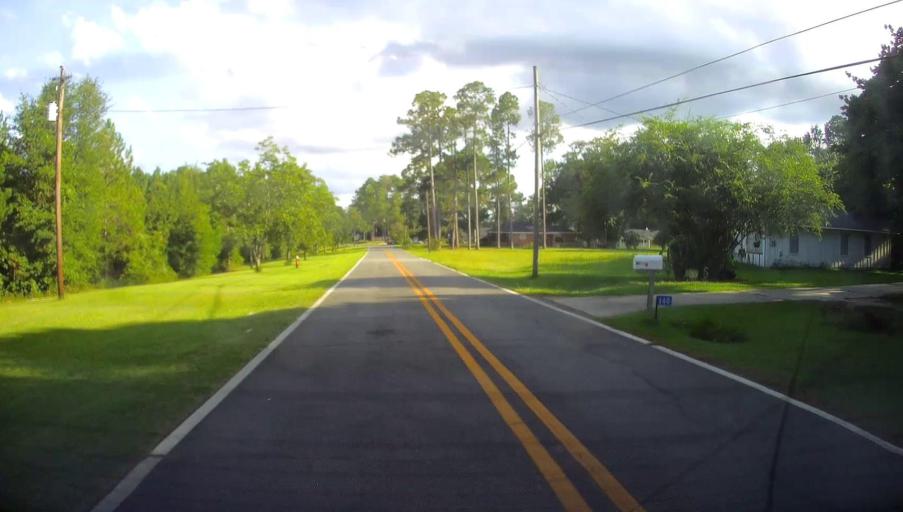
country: US
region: Georgia
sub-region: Crawford County
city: Roberta
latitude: 32.7129
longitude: -84.0183
